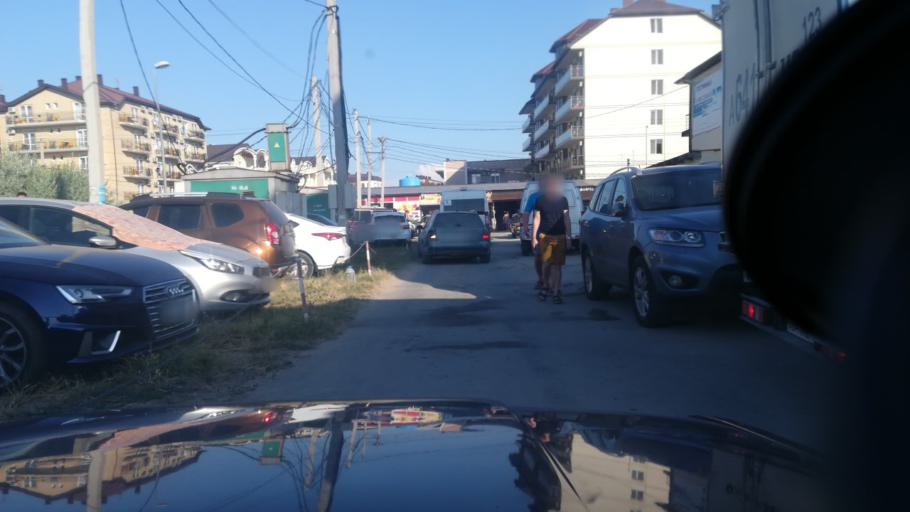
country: RU
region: Krasnodarskiy
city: Vityazevo
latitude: 44.9874
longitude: 37.2504
